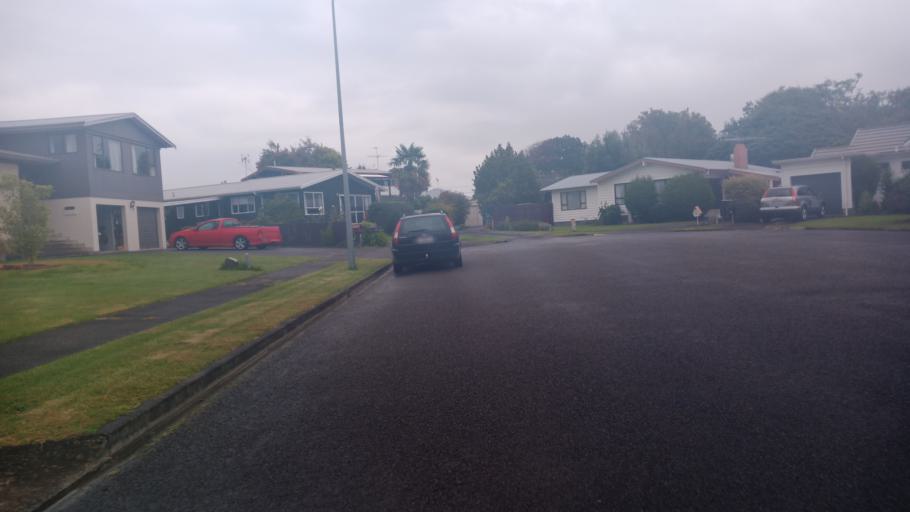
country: NZ
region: Gisborne
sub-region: Gisborne District
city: Gisborne
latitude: -38.6561
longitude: 178.0356
